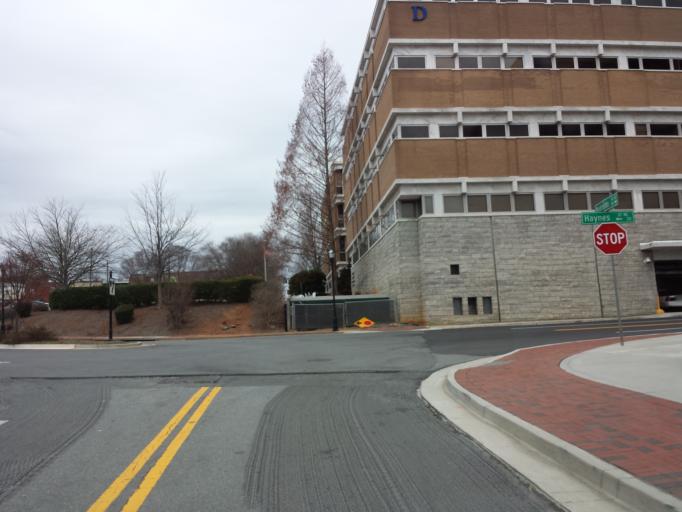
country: US
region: Georgia
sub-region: Cobb County
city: Marietta
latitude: 33.9522
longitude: -84.5468
